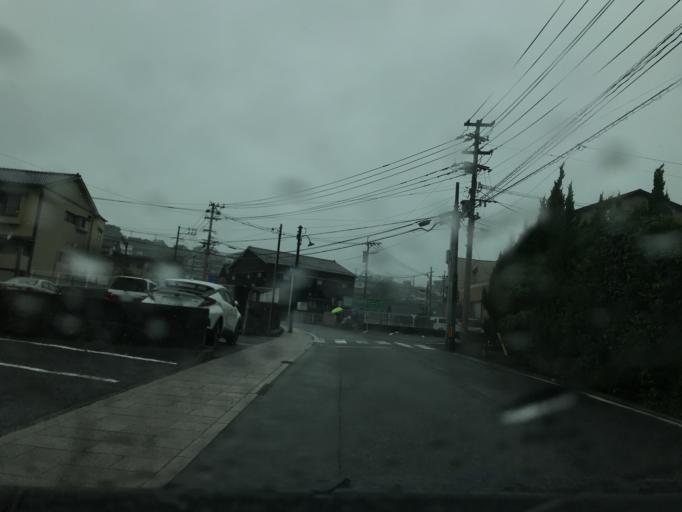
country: JP
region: Oita
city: Beppu
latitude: 33.3150
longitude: 131.4795
